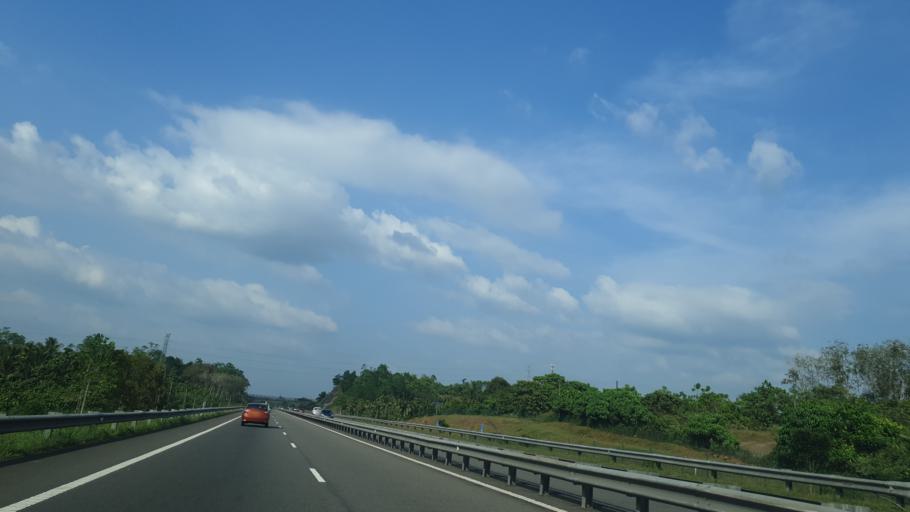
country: LK
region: Western
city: Horana South
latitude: 6.6684
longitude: 80.0041
